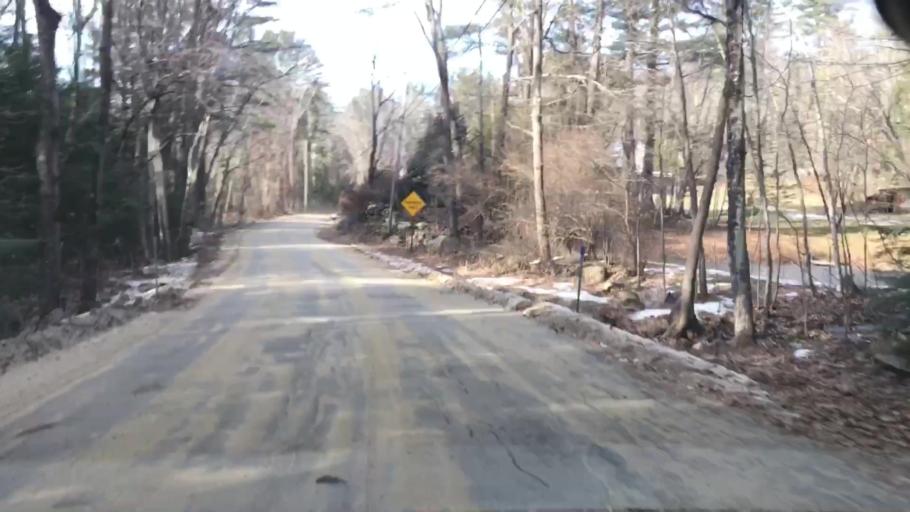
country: US
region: New Hampshire
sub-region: Hillsborough County
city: Mont Vernon
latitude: 42.9134
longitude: -71.6093
